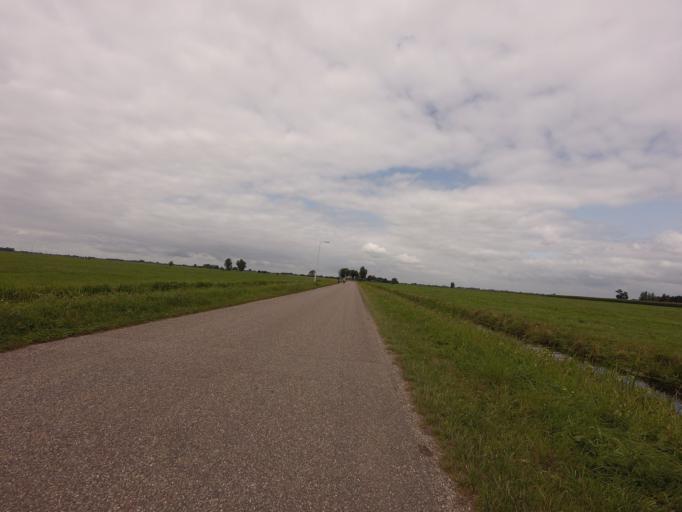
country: NL
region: South Holland
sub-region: Molenwaard
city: Liesveld
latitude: 51.8850
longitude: 4.7954
